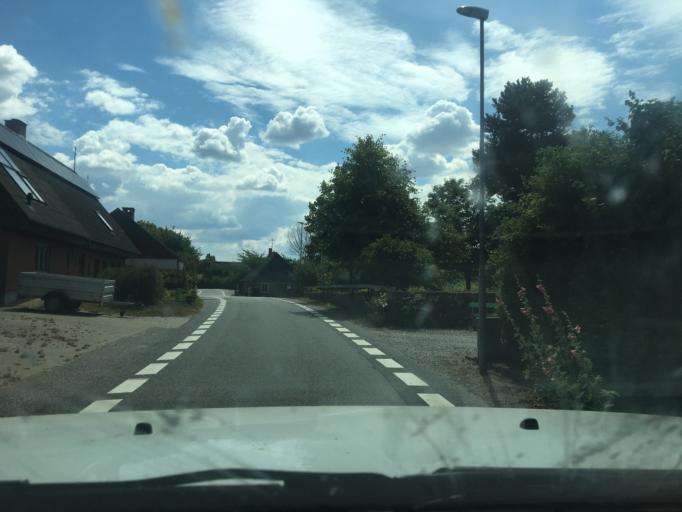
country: DK
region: Central Jutland
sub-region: Syddjurs Kommune
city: Hornslet
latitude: 56.3493
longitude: 10.2876
